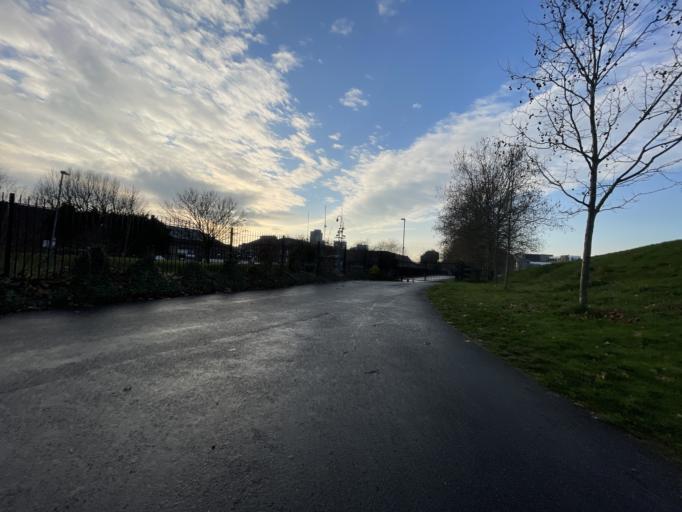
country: GB
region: England
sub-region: Greater London
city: Poplar
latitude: 51.5283
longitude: -0.0047
